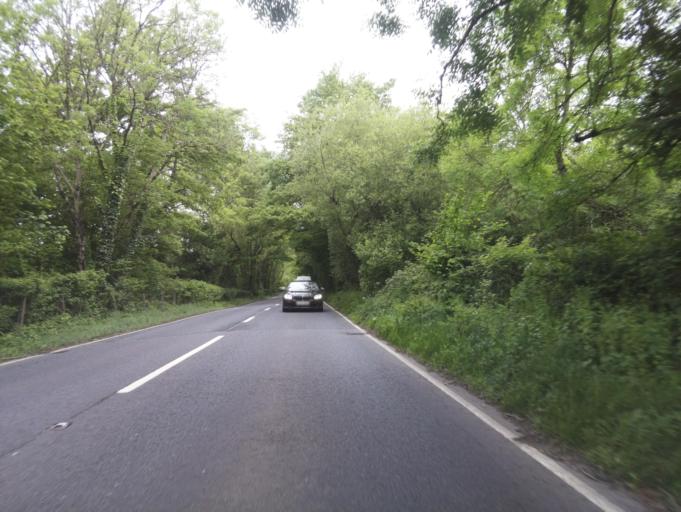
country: GB
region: England
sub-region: Devon
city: Colyton
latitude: 50.7888
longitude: -3.0982
